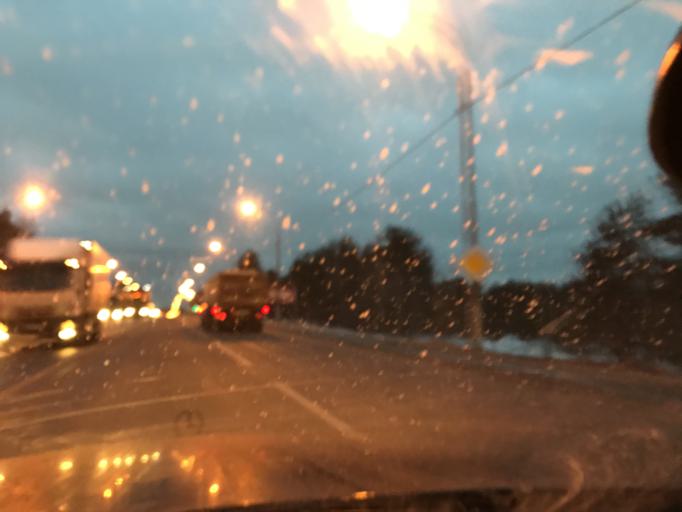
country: RU
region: Vladimir
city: Pokrov
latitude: 55.9205
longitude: 39.2108
